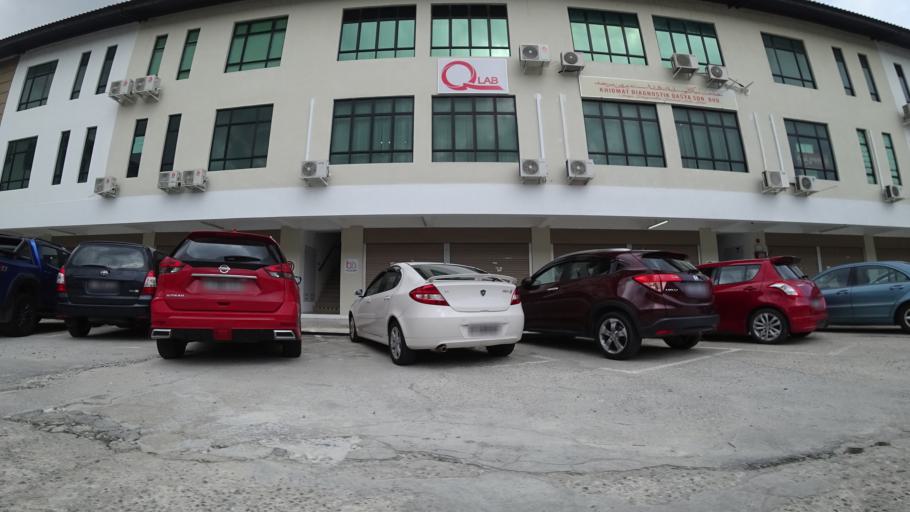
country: BN
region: Brunei and Muara
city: Bandar Seri Begawan
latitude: 4.9477
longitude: 114.9434
